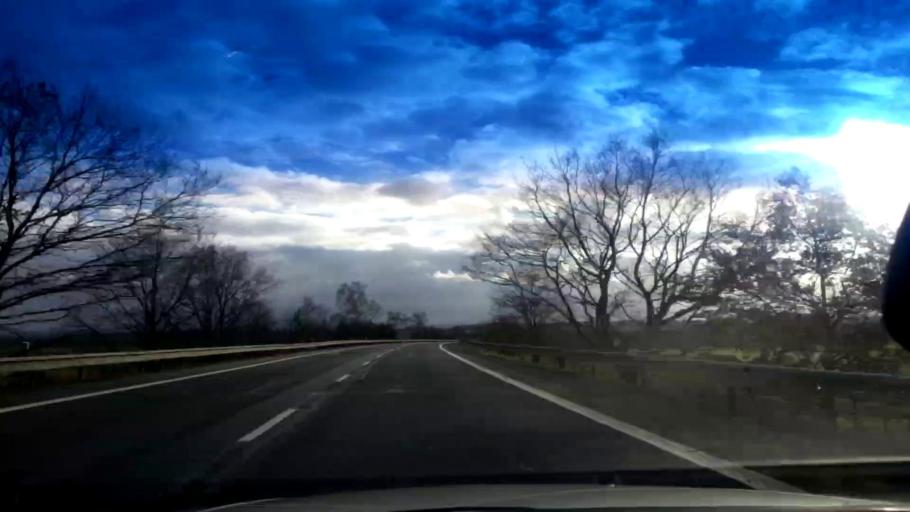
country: CZ
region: Karlovarsky
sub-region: Okres Cheb
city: Frantiskovy Lazne
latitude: 50.1186
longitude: 12.3722
